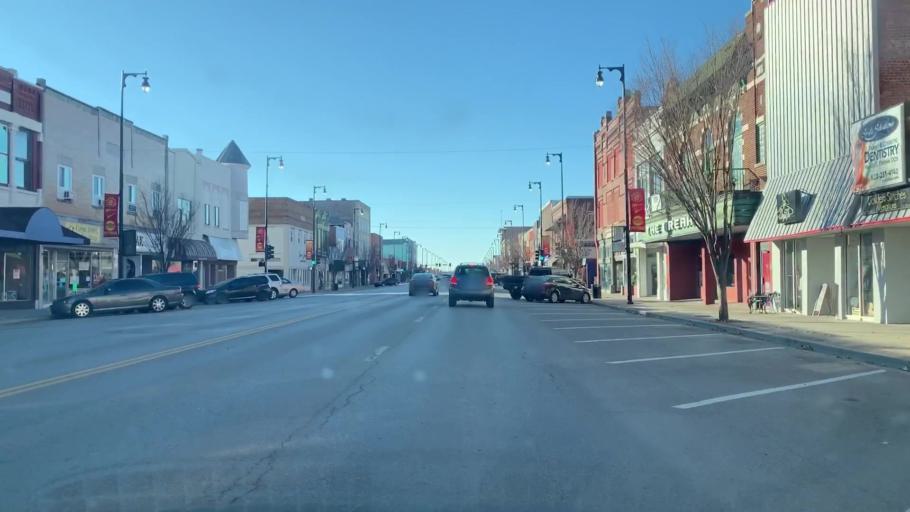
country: US
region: Kansas
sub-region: Crawford County
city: Pittsburg
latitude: 37.4137
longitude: -94.7049
